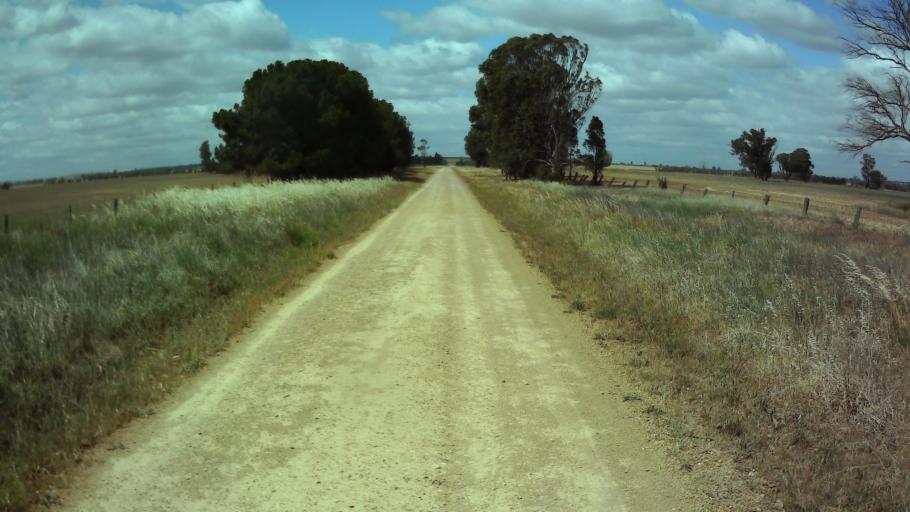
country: AU
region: New South Wales
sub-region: Weddin
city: Grenfell
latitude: -34.0493
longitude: 148.3323
